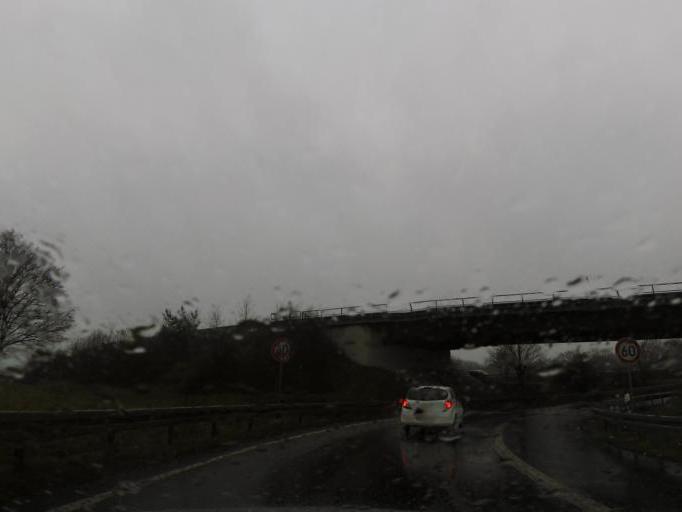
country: DE
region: Hesse
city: Niederrad
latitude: 50.0538
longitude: 8.6070
